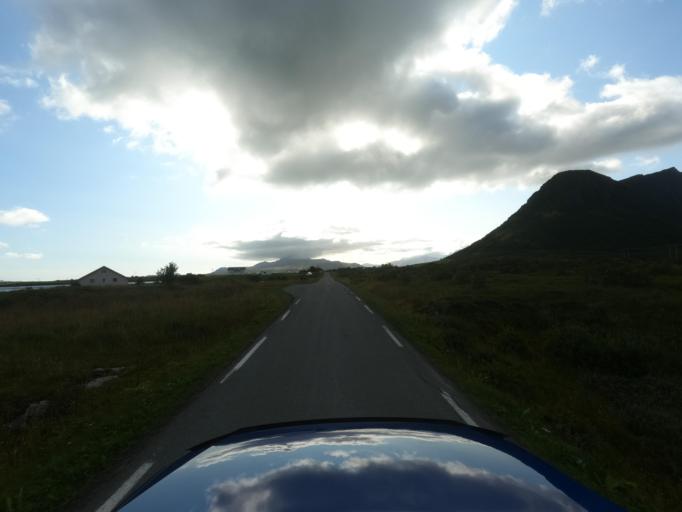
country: NO
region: Nordland
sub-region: Vestvagoy
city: Gravdal
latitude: 68.1679
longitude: 13.5499
